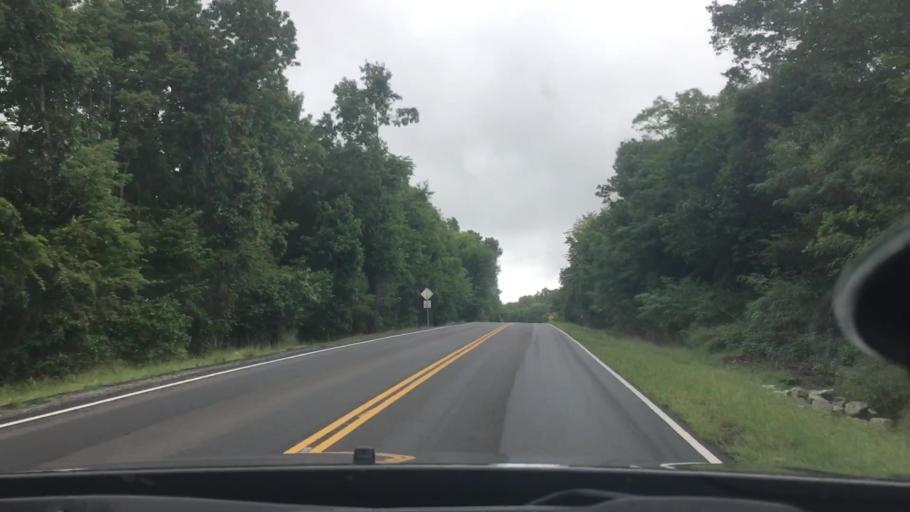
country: US
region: Oklahoma
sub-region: Sequoyah County
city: Vian
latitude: 35.6528
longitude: -94.9531
